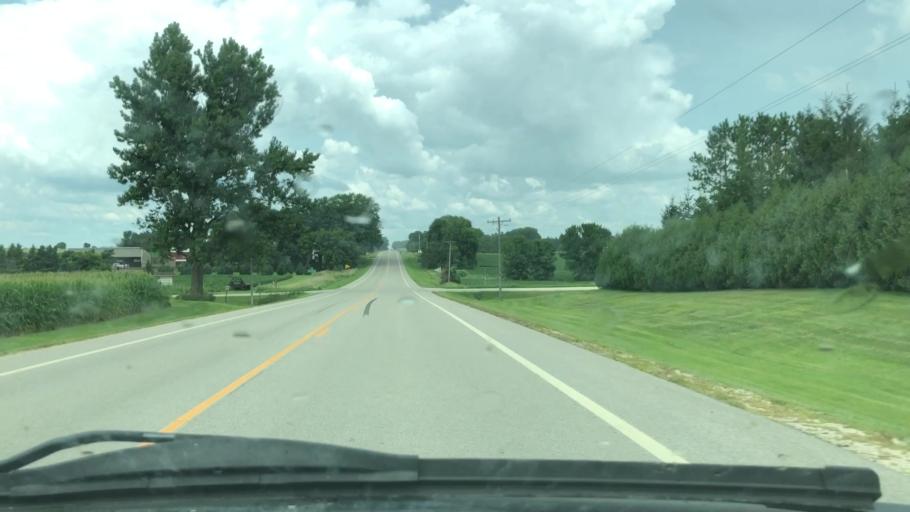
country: US
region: Minnesota
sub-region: Olmsted County
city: Stewartville
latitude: 43.8692
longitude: -92.5286
